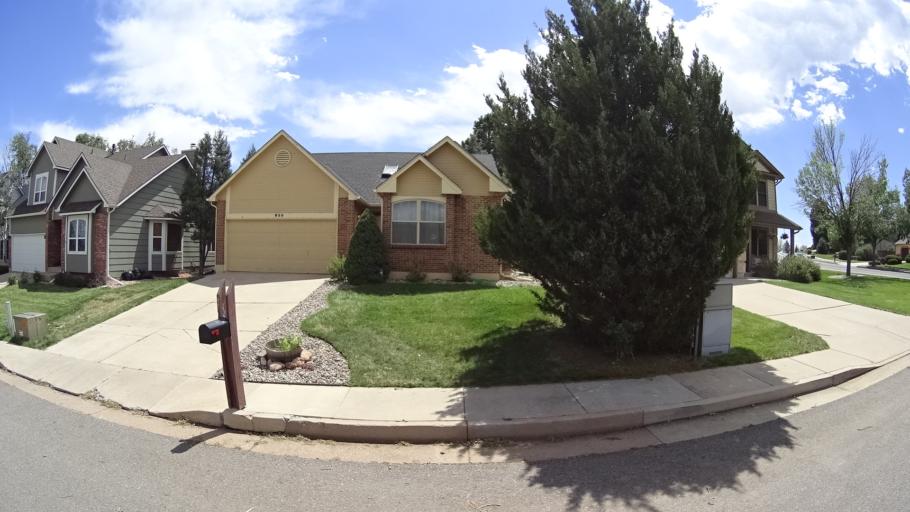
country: US
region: Colorado
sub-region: El Paso County
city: Stratmoor
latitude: 38.7699
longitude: -104.8173
